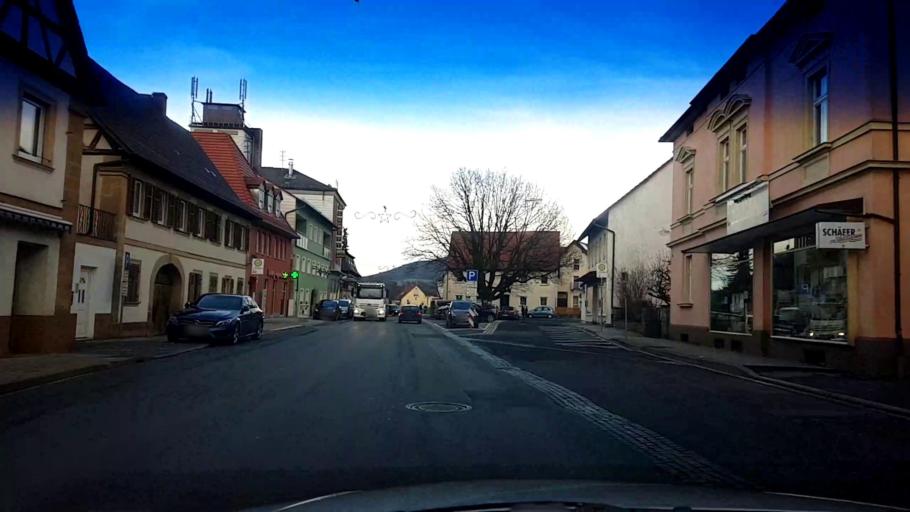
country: DE
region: Bavaria
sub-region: Upper Franconia
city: Schesslitz
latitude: 49.9767
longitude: 11.0355
